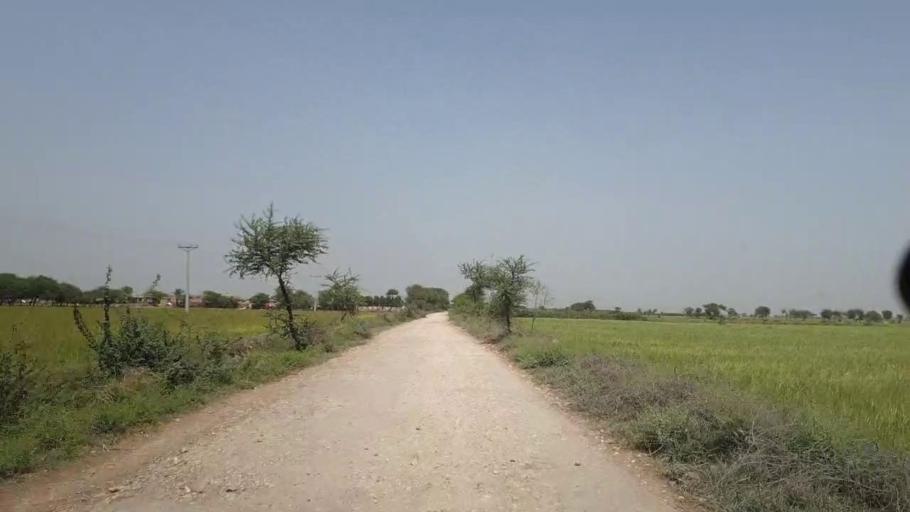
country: PK
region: Sindh
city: Matli
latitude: 25.0605
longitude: 68.6923
